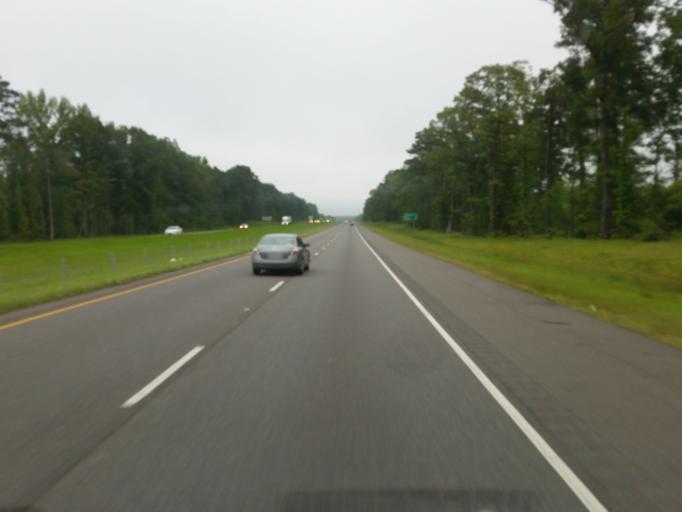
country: US
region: Louisiana
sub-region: Bossier Parish
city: Haughton
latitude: 32.5576
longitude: -93.5037
